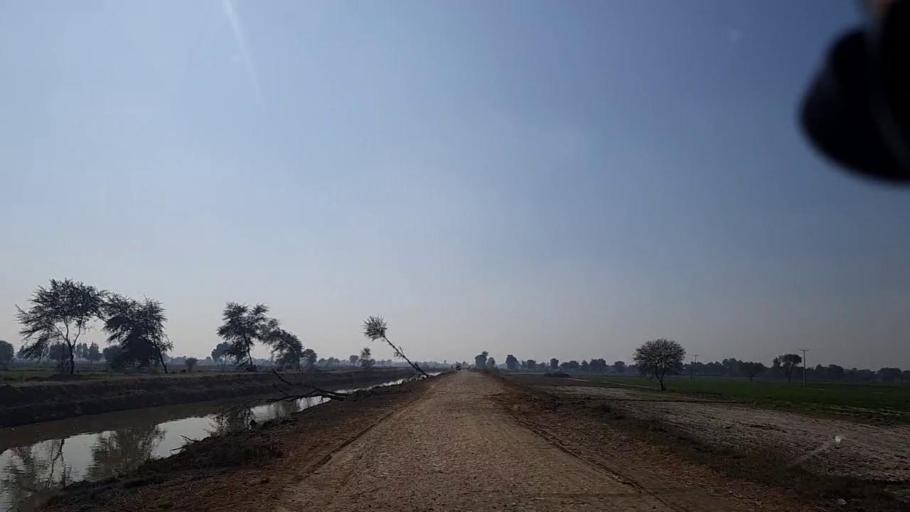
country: PK
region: Sindh
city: Khanpur
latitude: 27.8000
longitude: 69.4088
